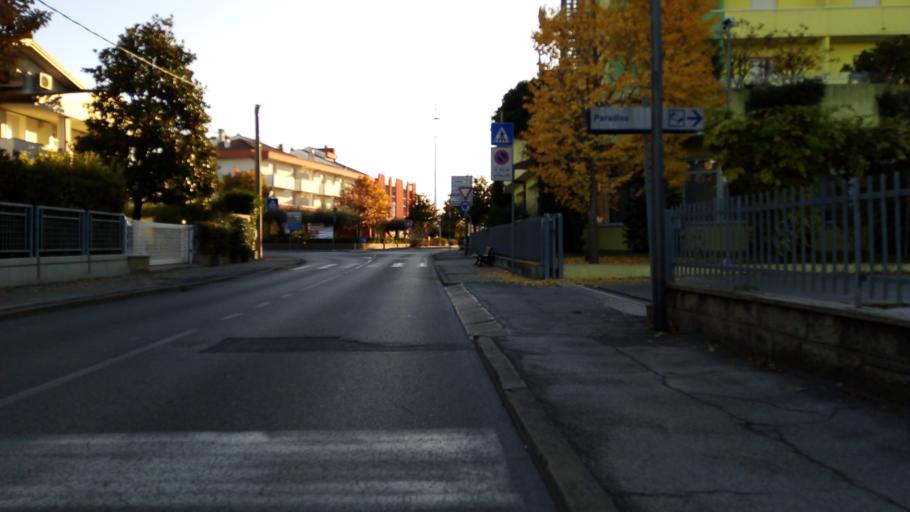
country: IT
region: Veneto
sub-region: Provincia di Padova
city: Abano Terme
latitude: 45.3486
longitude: 11.7891
